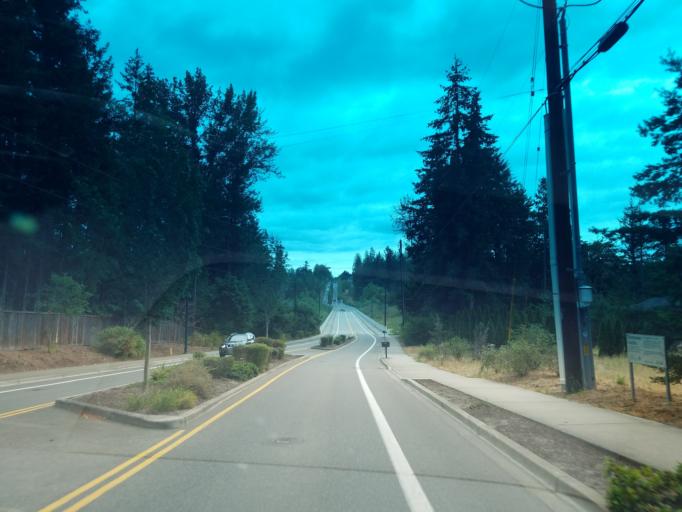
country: US
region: Washington
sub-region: King County
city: City of Sammamish
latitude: 47.6153
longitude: -122.0141
